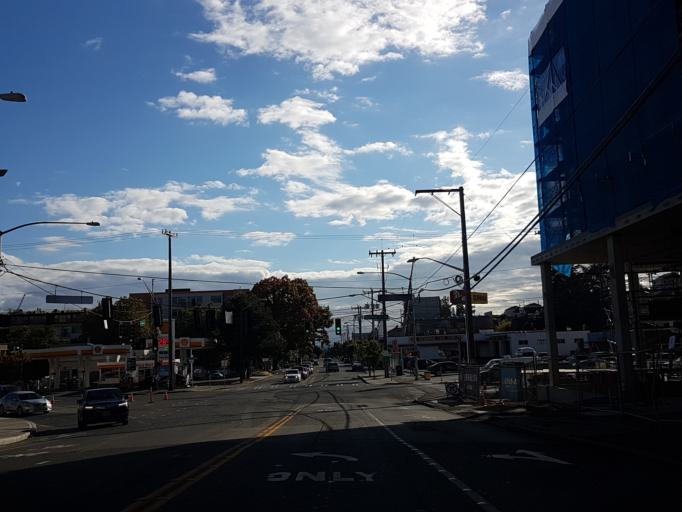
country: US
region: Washington
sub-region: King County
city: White Center
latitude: 47.5609
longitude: -122.3822
